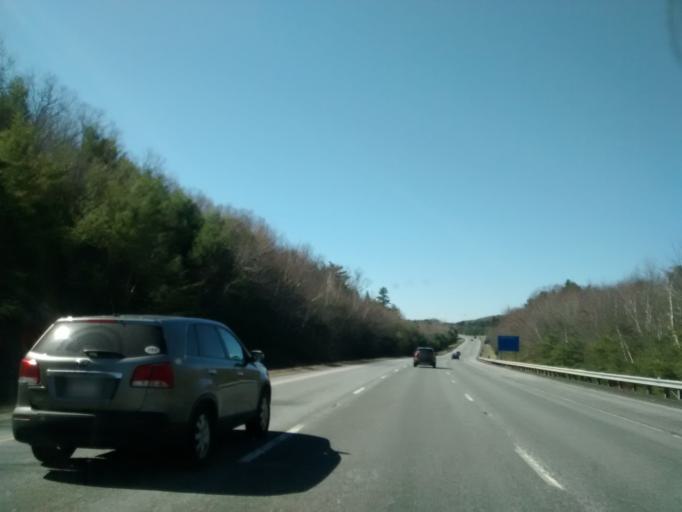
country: US
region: Massachusetts
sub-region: Worcester County
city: Sturbridge
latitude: 42.0766
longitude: -72.1009
